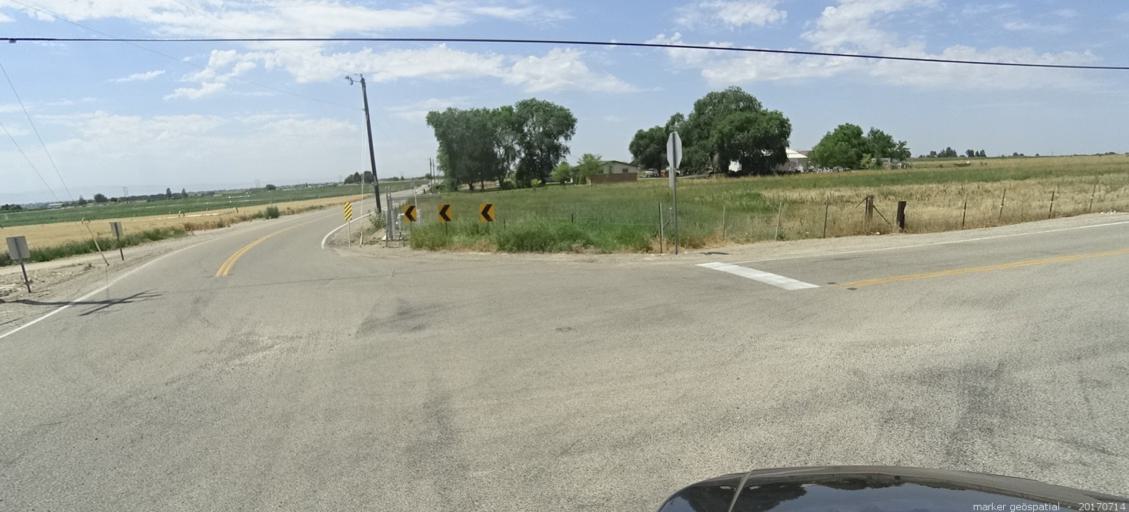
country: US
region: Idaho
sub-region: Ada County
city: Kuna
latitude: 43.5246
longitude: -116.3543
